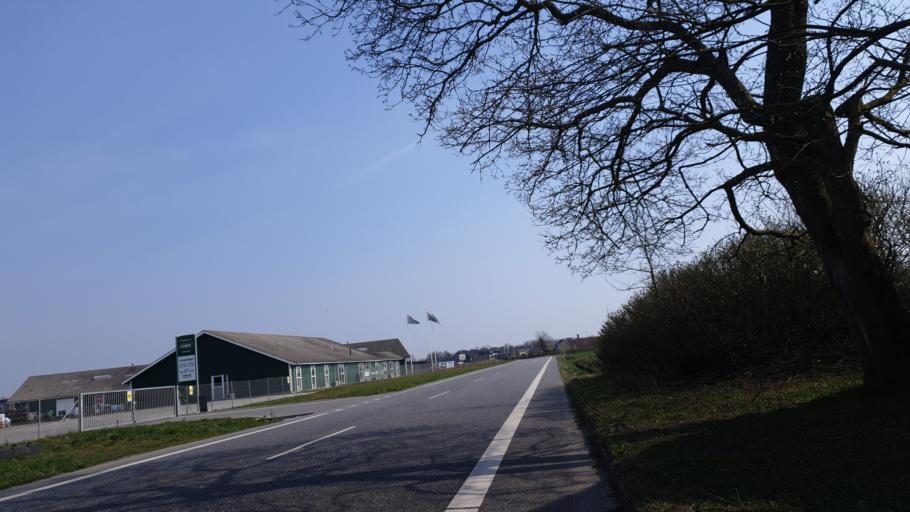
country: DK
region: Central Jutland
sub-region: Hedensted Kommune
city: Hedensted
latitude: 55.7838
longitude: 9.6845
